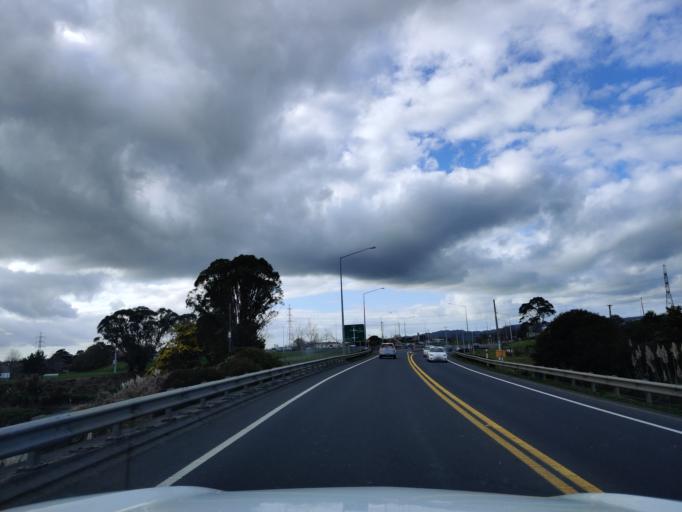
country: NZ
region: Auckland
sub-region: Auckland
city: Papakura
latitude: -37.1099
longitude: 174.9430
